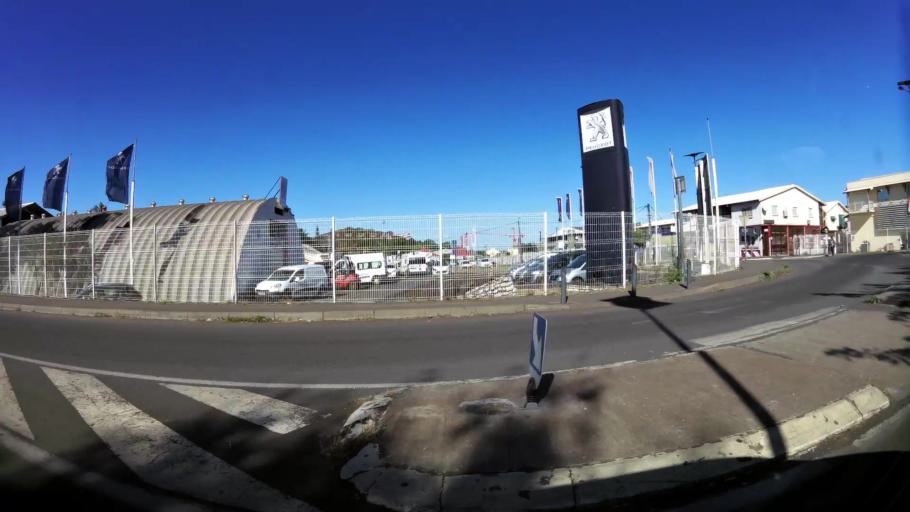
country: YT
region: Mamoudzou
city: Mamoudzou
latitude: -12.7710
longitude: 45.2236
